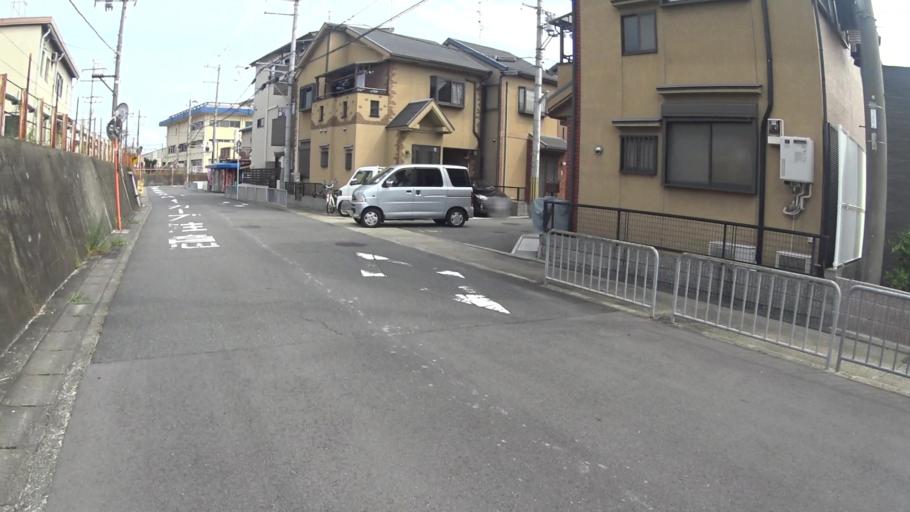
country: JP
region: Kyoto
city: Muko
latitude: 34.9392
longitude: 135.7097
